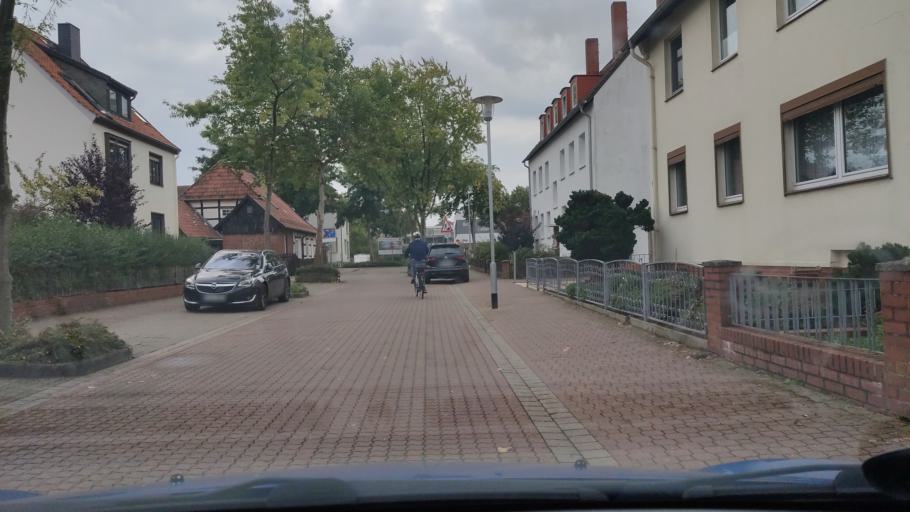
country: DE
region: Lower Saxony
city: Auf der Horst
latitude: 52.3997
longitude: 9.6426
